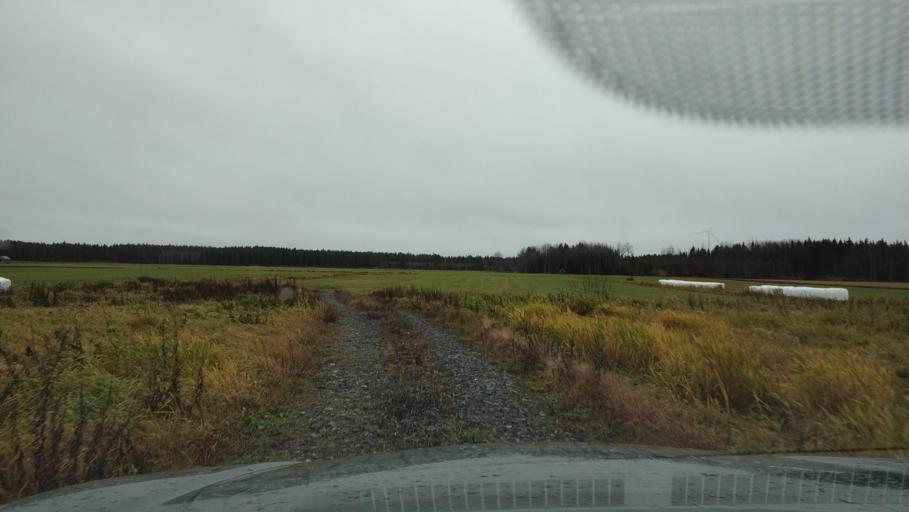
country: FI
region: Southern Ostrobothnia
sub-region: Suupohja
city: Karijoki
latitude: 62.2280
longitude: 21.5527
